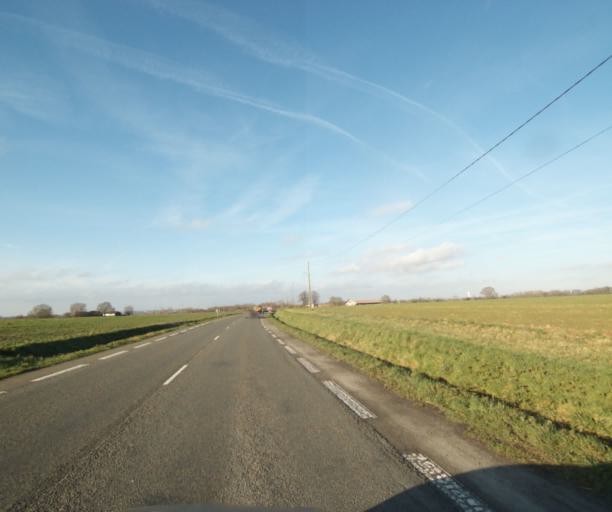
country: FR
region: Nord-Pas-de-Calais
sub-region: Departement du Nord
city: Saultain
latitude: 50.3269
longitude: 3.5610
